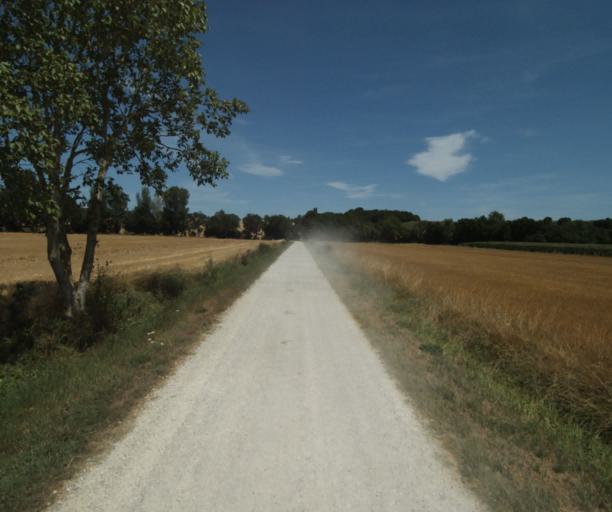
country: FR
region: Midi-Pyrenees
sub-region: Departement de la Haute-Garonne
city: Revel
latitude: 43.4997
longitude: 2.0391
